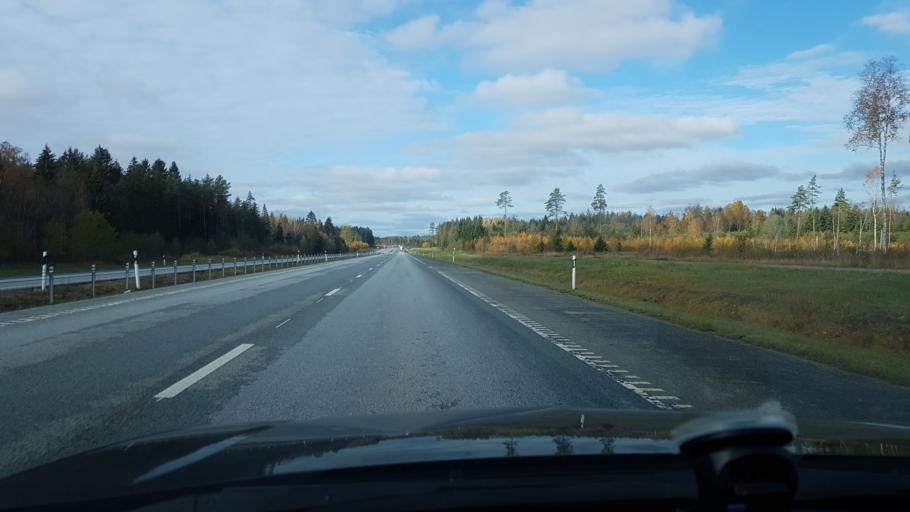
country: EE
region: Laeaene-Virumaa
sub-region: Kadrina vald
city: Kadrina
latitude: 59.4549
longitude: 26.0514
